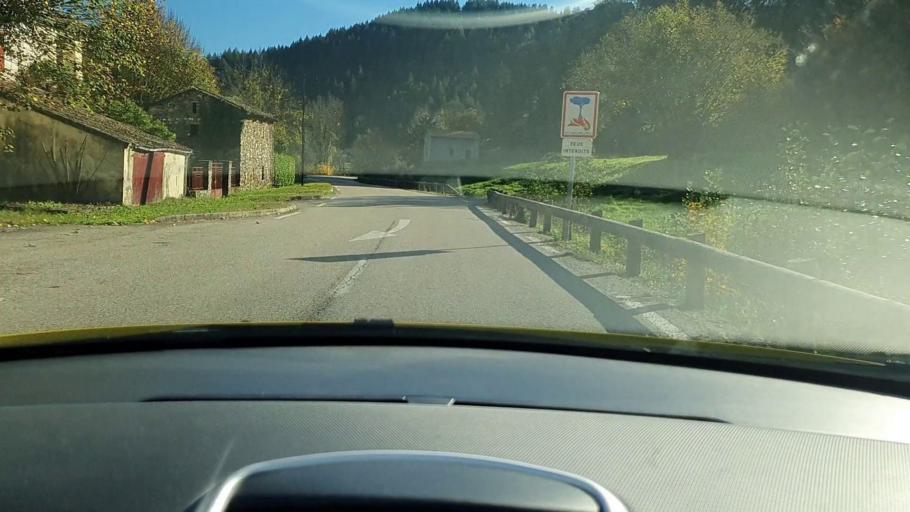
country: FR
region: Languedoc-Roussillon
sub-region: Departement du Gard
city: Lasalle
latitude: 44.1150
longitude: 3.7662
